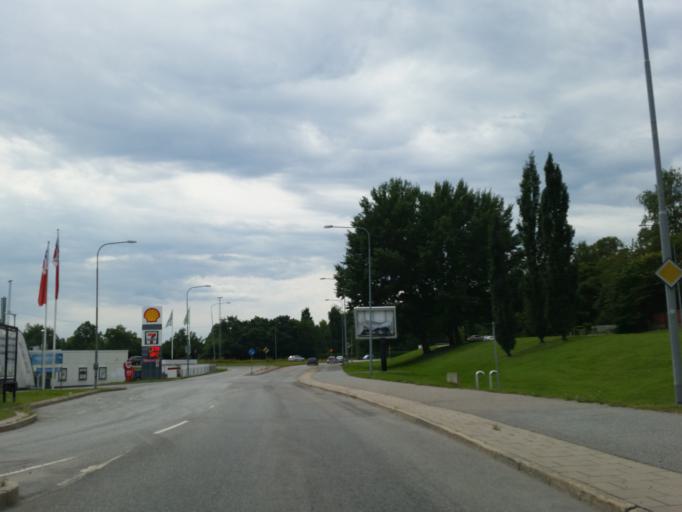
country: SE
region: Stockholm
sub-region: Sodertalje Kommun
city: Soedertaelje
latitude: 59.2039
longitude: 17.6443
